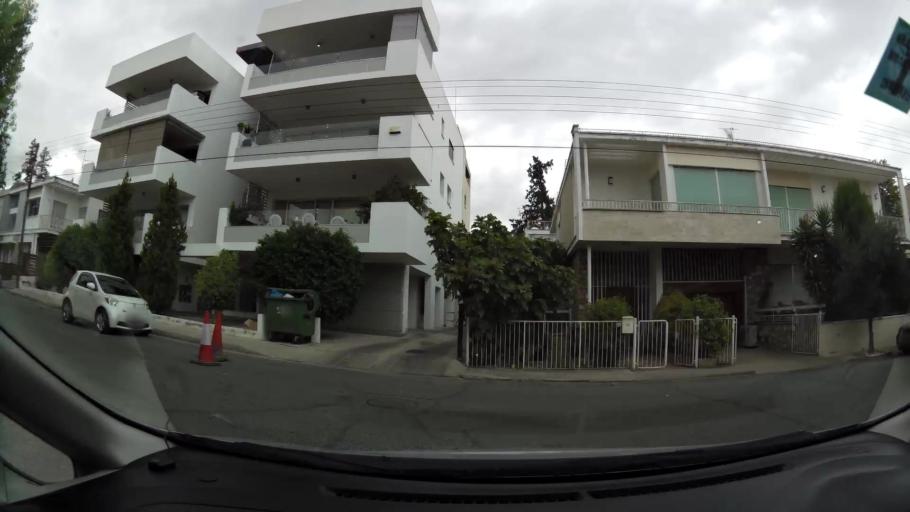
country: CY
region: Lefkosia
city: Nicosia
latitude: 35.1563
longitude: 33.3526
